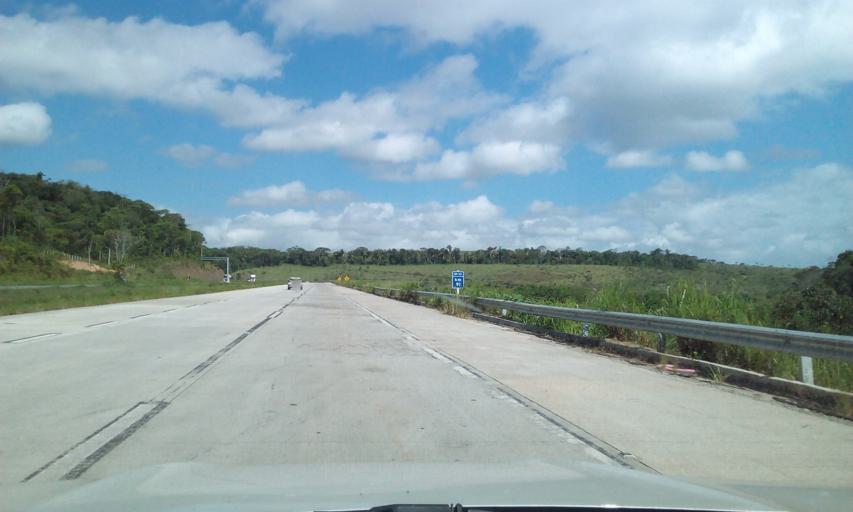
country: BR
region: Alagoas
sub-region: Rio Largo
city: Rio Largo
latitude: -9.5032
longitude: -35.9134
